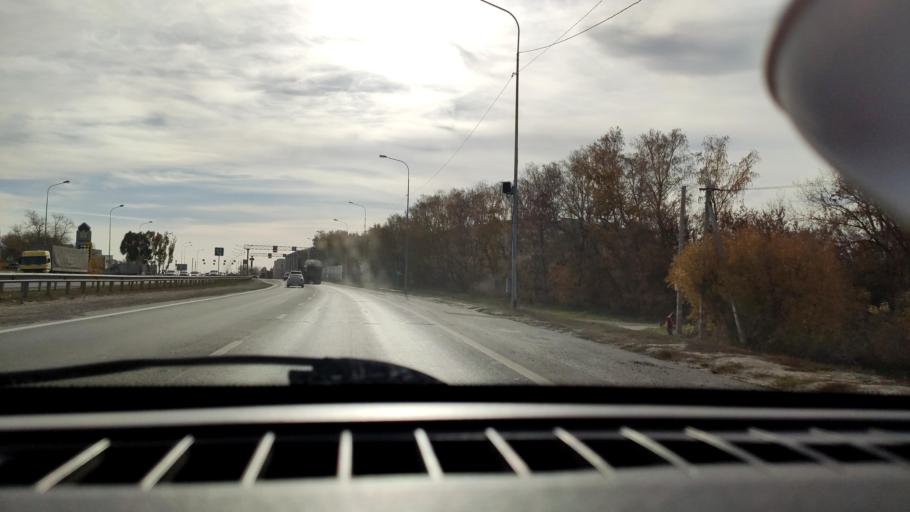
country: RU
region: Samara
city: Petra-Dubrava
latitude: 53.3133
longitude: 50.2926
